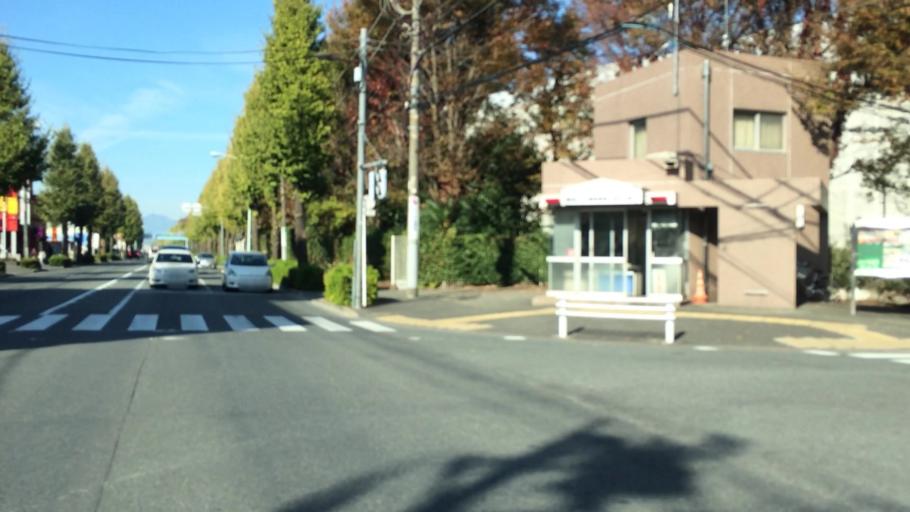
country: JP
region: Tokyo
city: Hino
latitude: 35.6923
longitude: 139.3929
